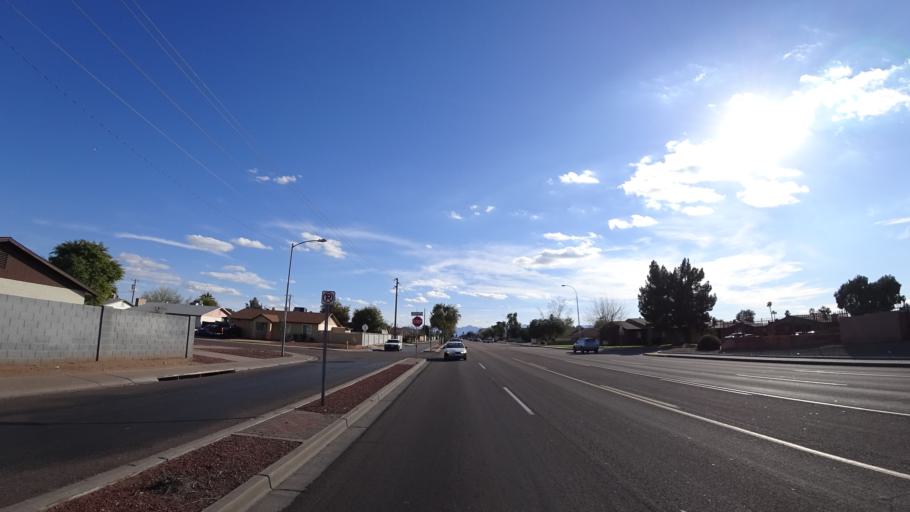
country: US
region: Arizona
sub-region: Maricopa County
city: Tolleson
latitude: 33.4914
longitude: -112.2377
